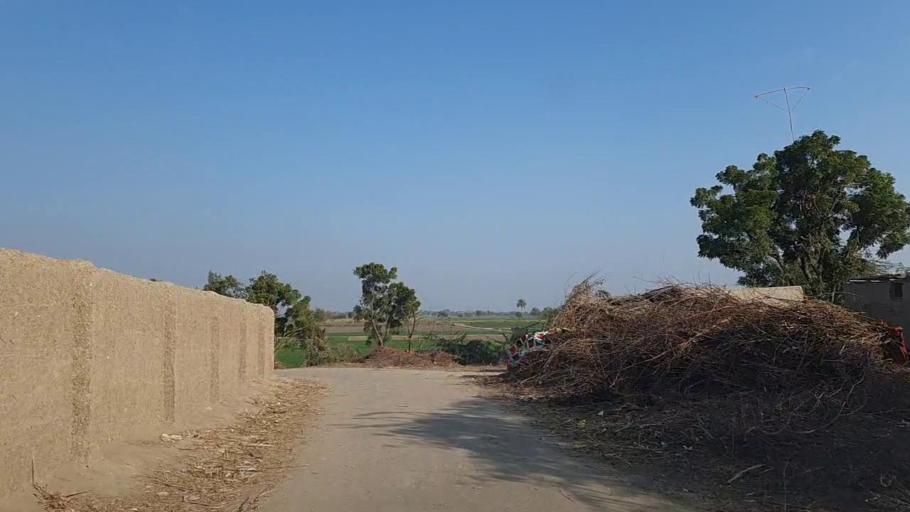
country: PK
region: Sindh
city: Nawabshah
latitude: 26.3747
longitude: 68.4768
